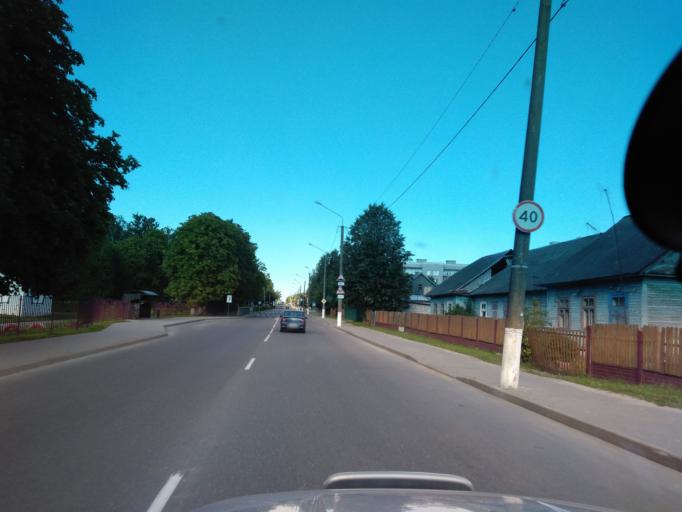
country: BY
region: Minsk
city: Dzyarzhynsk
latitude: 53.6818
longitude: 27.1246
